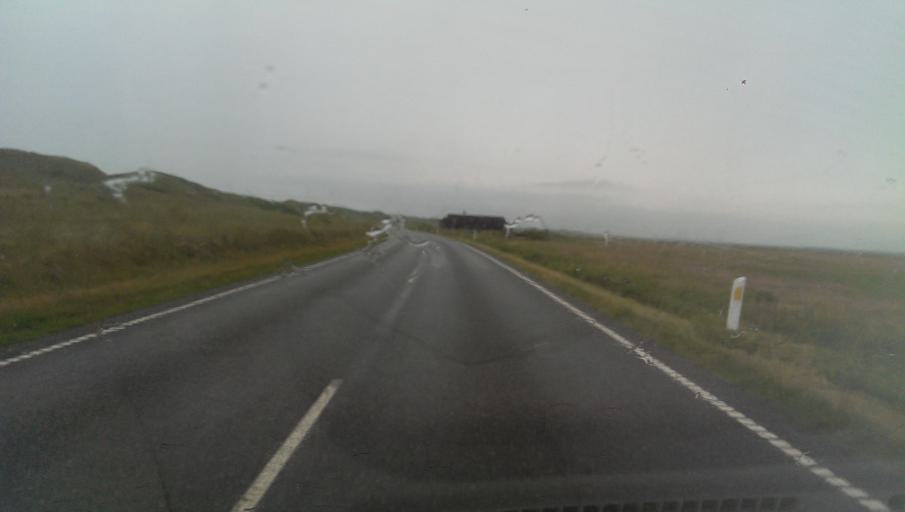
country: DK
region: Central Jutland
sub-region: Ringkobing-Skjern Kommune
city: Ringkobing
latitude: 56.1817
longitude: 8.1274
